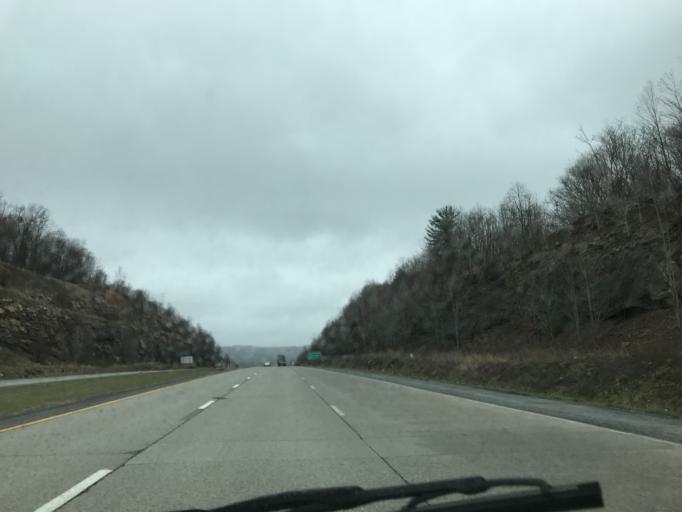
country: US
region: West Virginia
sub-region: Raleigh County
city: Shady Spring
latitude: 37.7693
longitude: -80.9847
